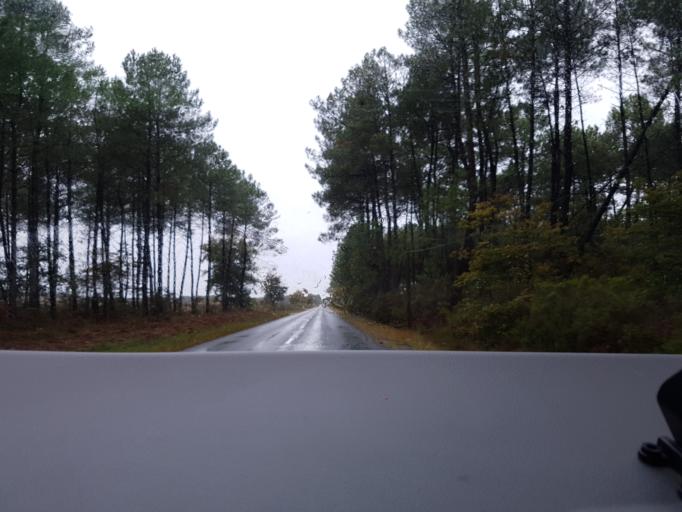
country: FR
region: Aquitaine
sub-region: Departement de la Gironde
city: Belin-Beliet
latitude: 44.5108
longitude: -0.7332
